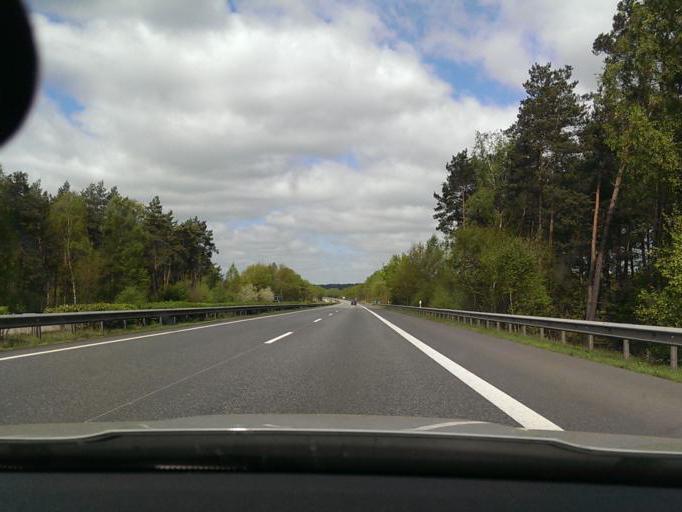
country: DE
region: Lower Saxony
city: Kirchlinteln
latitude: 52.9189
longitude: 9.3553
